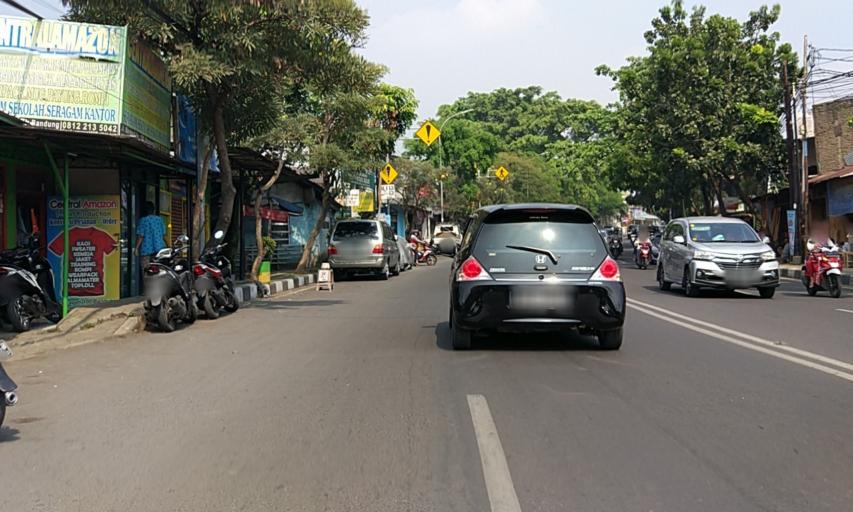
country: ID
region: West Java
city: Bandung
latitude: -6.8994
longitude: 107.6306
